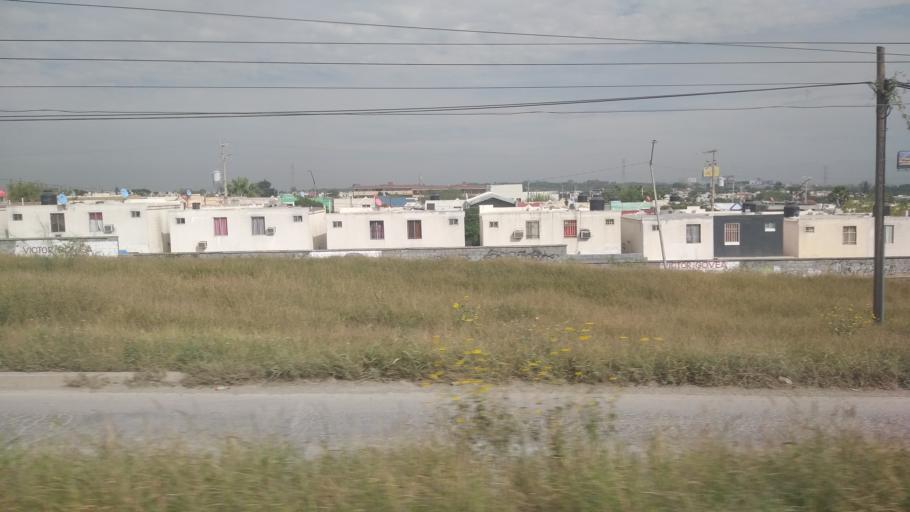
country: MX
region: Nuevo Leon
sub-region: Apodaca
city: Loma la Paz
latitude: 25.7022
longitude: -100.1434
